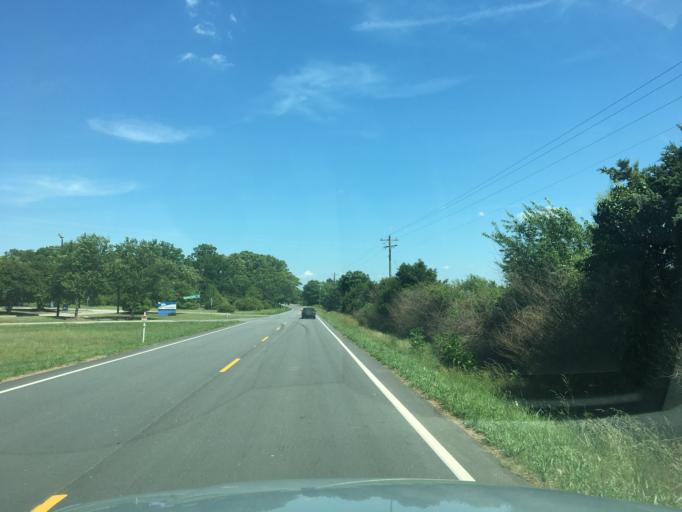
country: US
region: Georgia
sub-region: Hart County
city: Reed Creek
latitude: 34.5112
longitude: -82.9783
